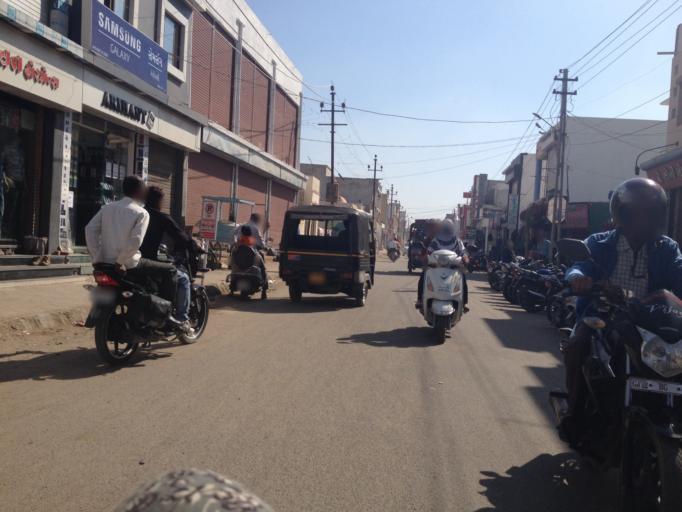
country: IN
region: Gujarat
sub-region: Kachchh
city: Anjar
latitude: 23.1123
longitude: 70.0283
